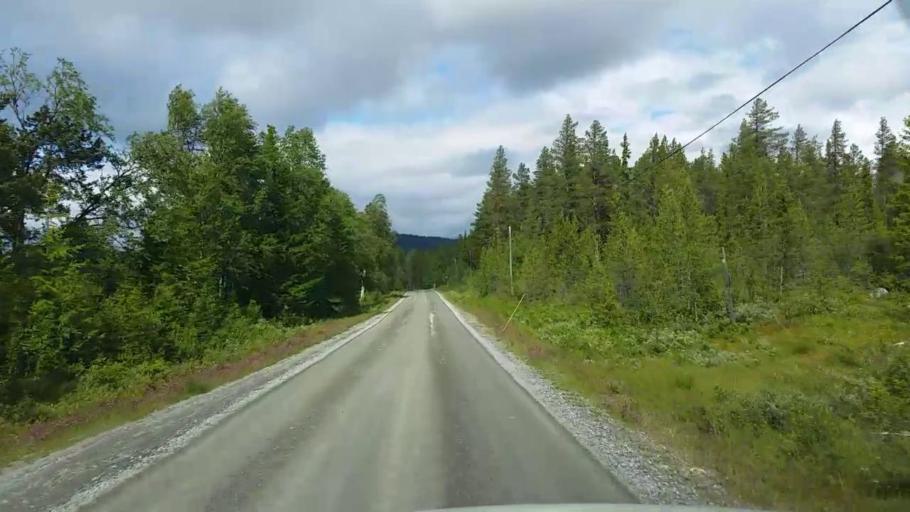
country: NO
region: Hedmark
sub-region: Engerdal
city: Engerdal
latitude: 62.4156
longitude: 12.6776
